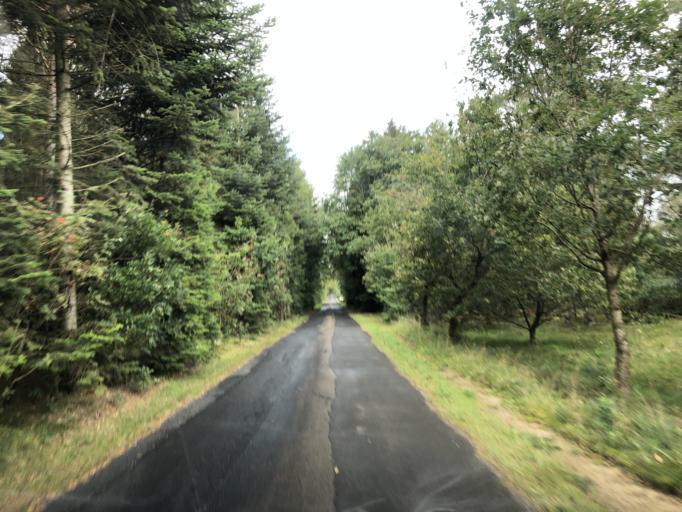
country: DK
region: Central Jutland
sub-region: Holstebro Kommune
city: Ulfborg
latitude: 56.3044
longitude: 8.4353
